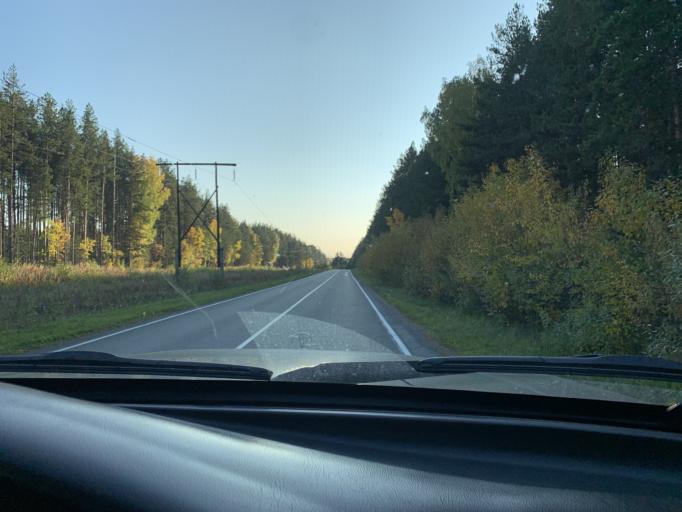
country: RU
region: Sverdlovsk
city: Verkhneye Dubrovo
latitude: 56.8669
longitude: 61.0930
